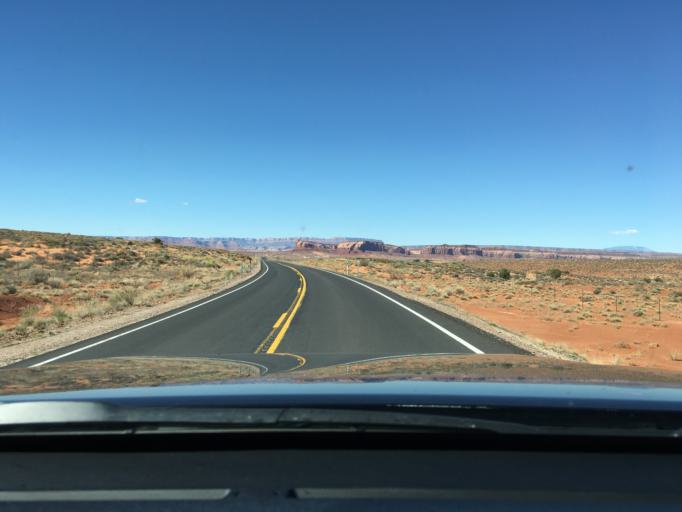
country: US
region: Arizona
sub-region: Navajo County
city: Kayenta
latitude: 37.0332
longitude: -110.1137
